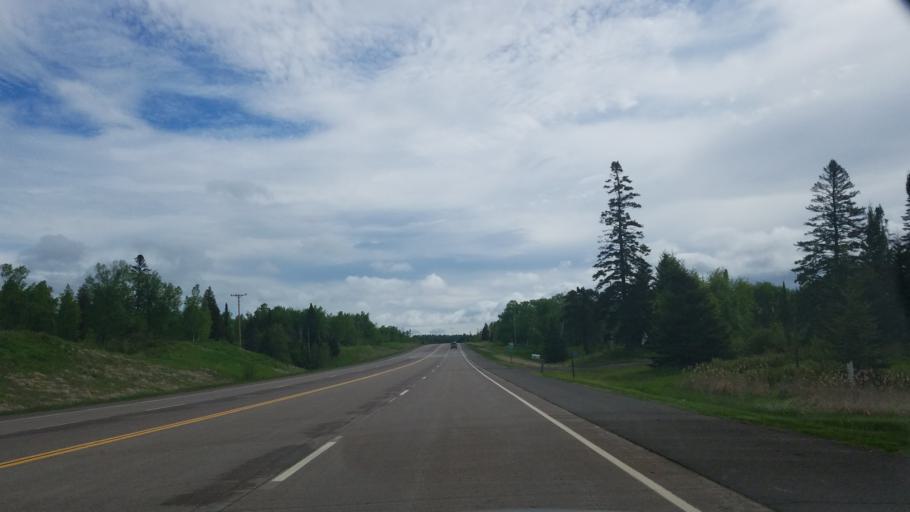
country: US
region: Minnesota
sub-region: Lake County
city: Two Harbors
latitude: 47.1288
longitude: -91.4885
